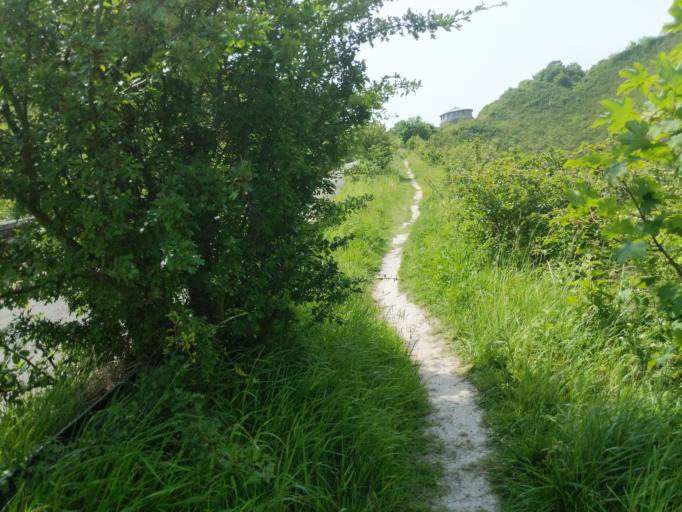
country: GB
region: England
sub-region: Kent
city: Folkestone
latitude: 51.0926
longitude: 1.2013
